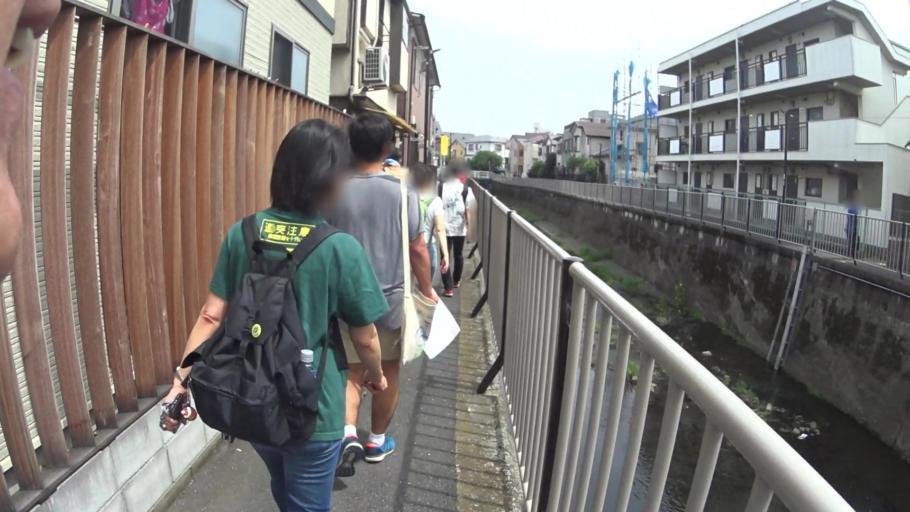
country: JP
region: Tokyo
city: Musashino
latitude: 35.7081
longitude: 139.5988
